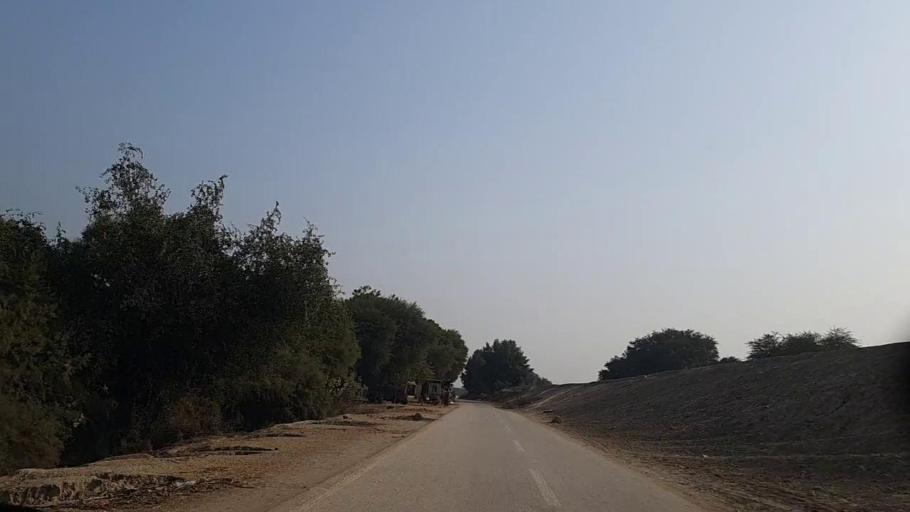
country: PK
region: Sindh
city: Sann
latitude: 26.1566
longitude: 68.1174
